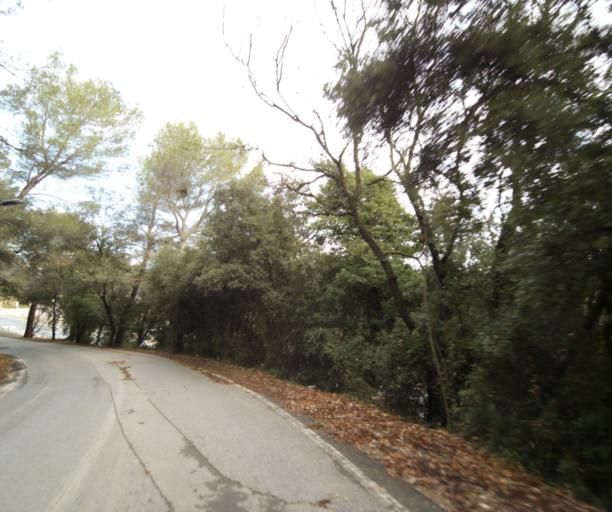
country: FR
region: Provence-Alpes-Cote d'Azur
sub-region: Departement du Var
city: Trans-en-Provence
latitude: 43.4939
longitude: 6.4951
